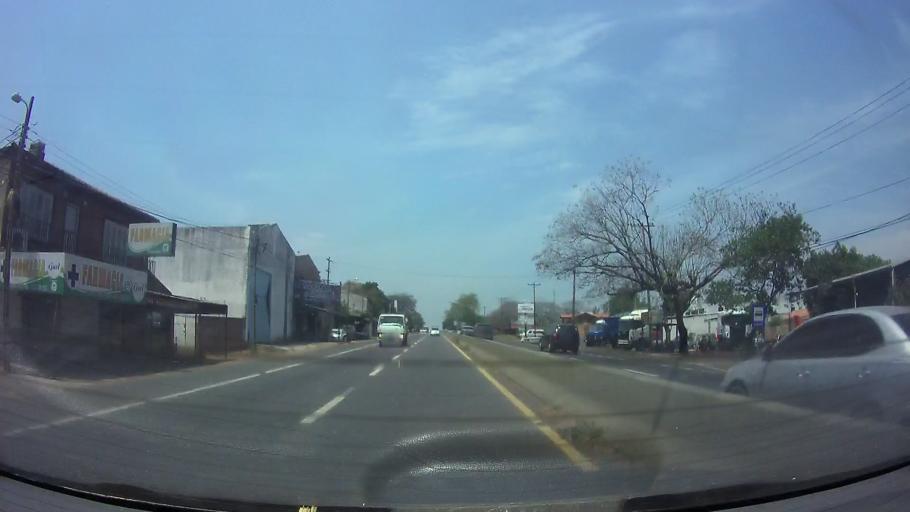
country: PY
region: Central
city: Capiata
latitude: -25.3782
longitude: -57.3935
